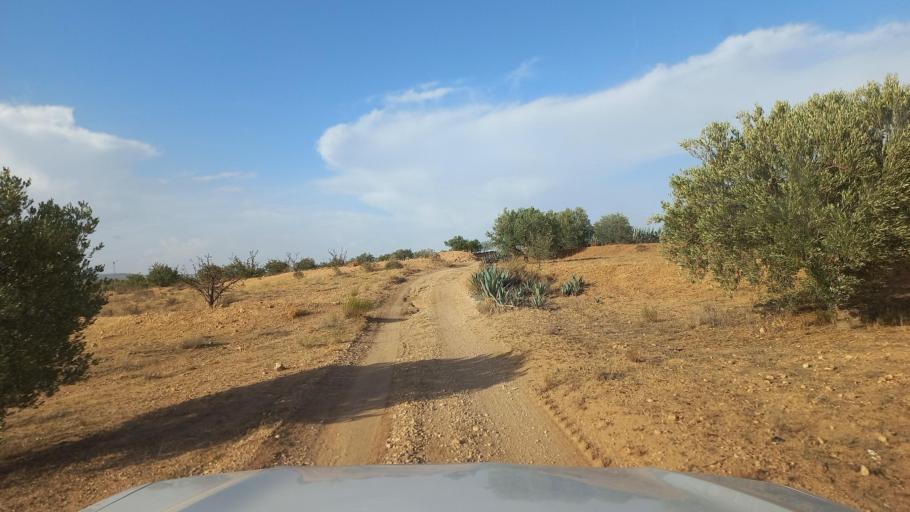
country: TN
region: Al Qasrayn
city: Kasserine
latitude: 35.2366
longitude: 8.9163
